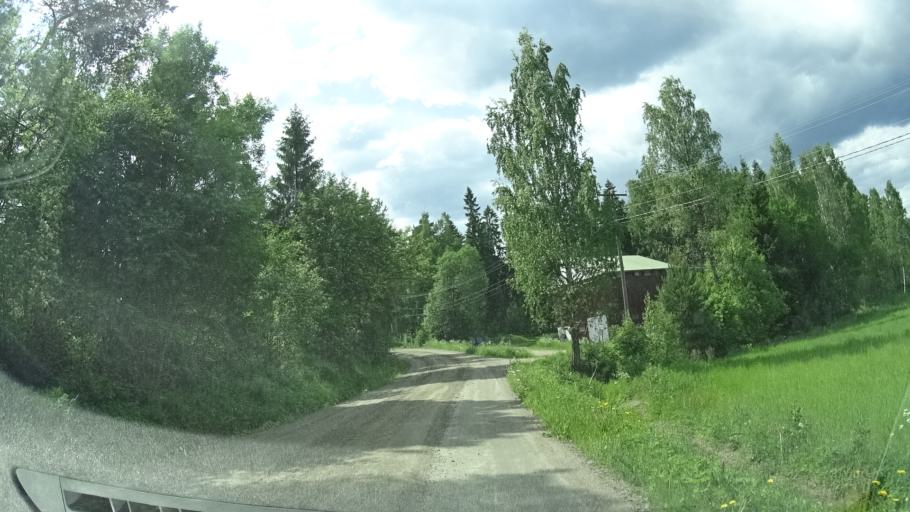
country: FI
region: Uusimaa
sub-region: Helsinki
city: Siuntio
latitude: 60.2180
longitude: 24.2922
